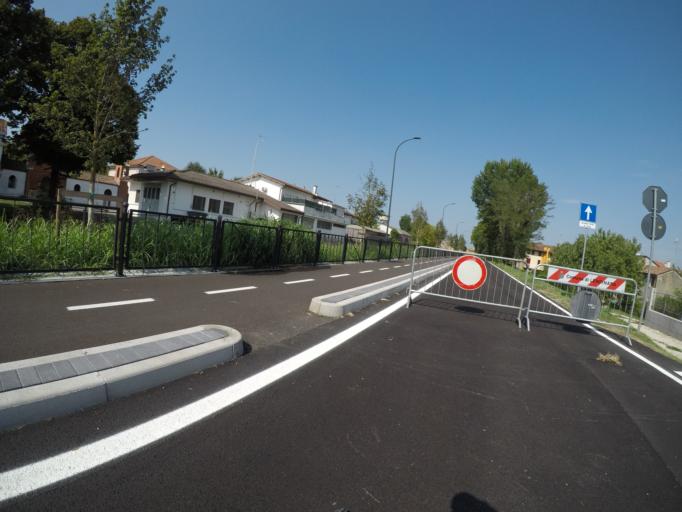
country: IT
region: Veneto
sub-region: Provincia di Rovigo
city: Lendinara
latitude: 45.0847
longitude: 11.5928
